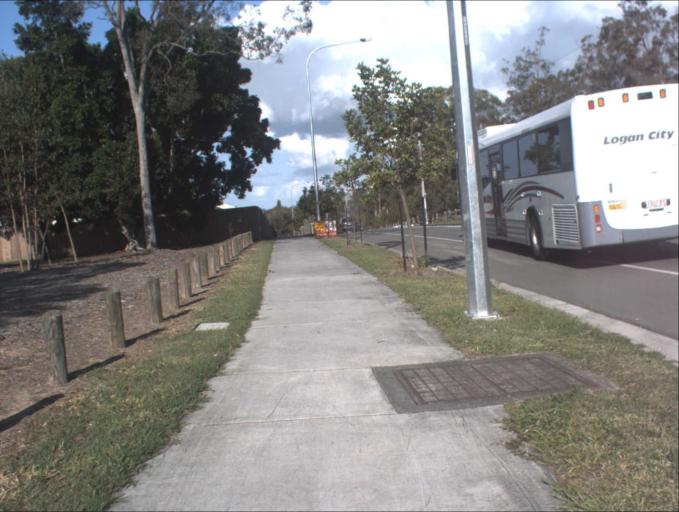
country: AU
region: Queensland
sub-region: Logan
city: Park Ridge South
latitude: -27.6885
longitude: 153.0456
